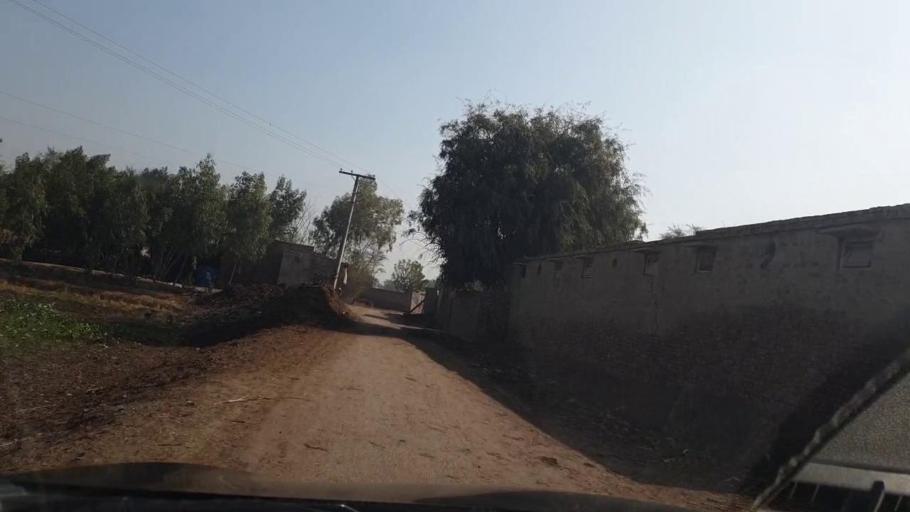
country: PK
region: Sindh
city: Ubauro
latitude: 28.1126
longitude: 69.7397
